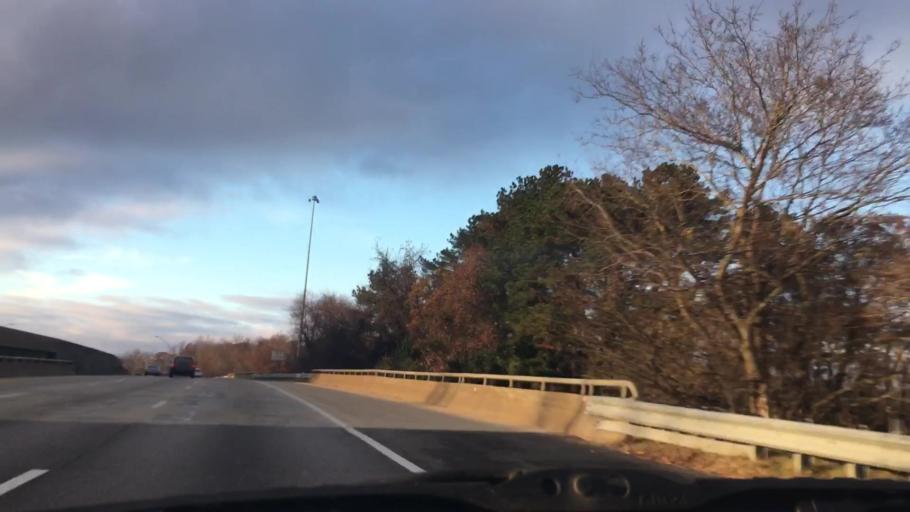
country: US
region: Virginia
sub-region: City of Norfolk
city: Norfolk
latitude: 36.8748
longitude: -76.1971
